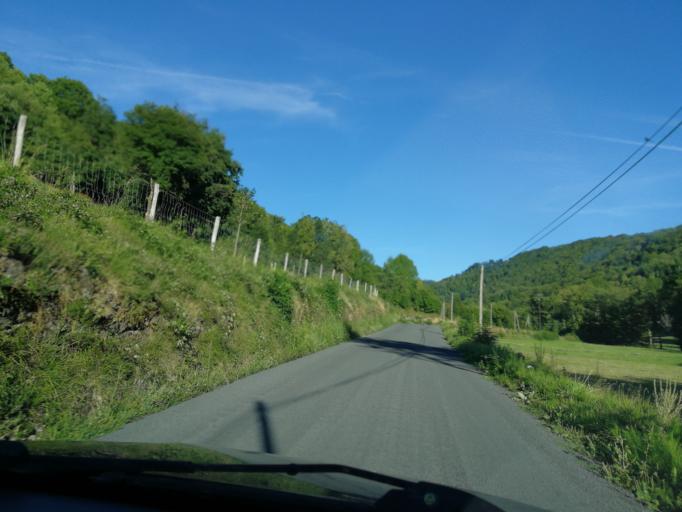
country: FR
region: Auvergne
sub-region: Departement du Cantal
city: Saint-Cernin
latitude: 45.1030
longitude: 2.5301
